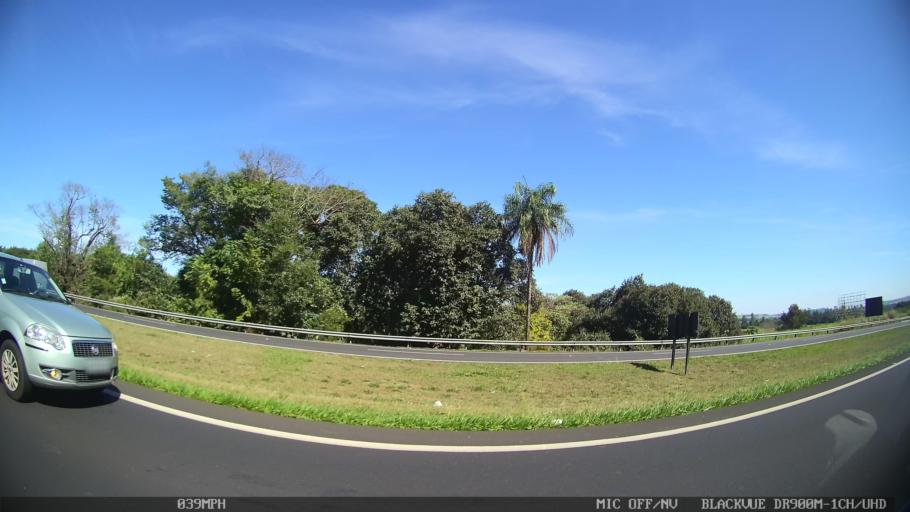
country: BR
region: Sao Paulo
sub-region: Santa Rita Do Passa Quatro
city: Santa Rita do Passa Quatro
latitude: -21.7485
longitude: -47.5727
